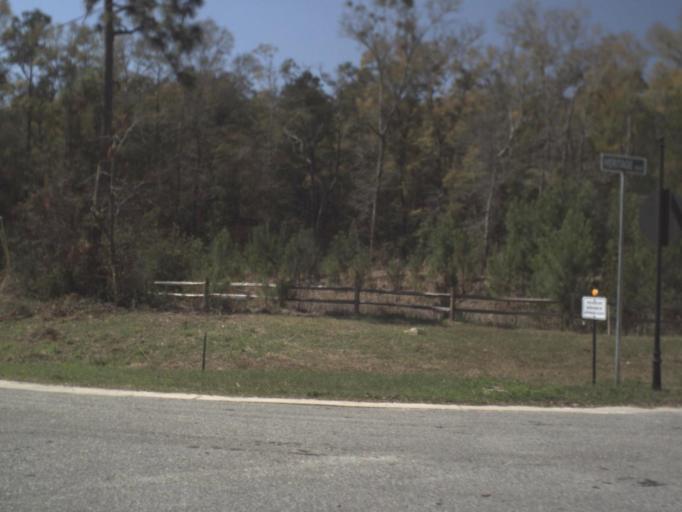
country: US
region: Florida
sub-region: Jefferson County
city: Monticello
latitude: 30.4935
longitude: -84.0262
